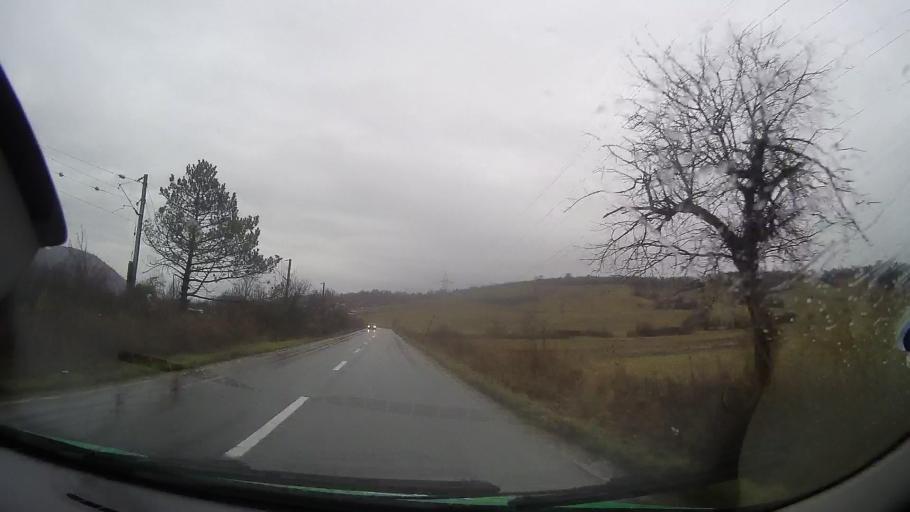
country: RO
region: Bistrita-Nasaud
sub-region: Municipiul Bistrita
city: Viisoara
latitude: 47.0465
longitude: 24.4639
